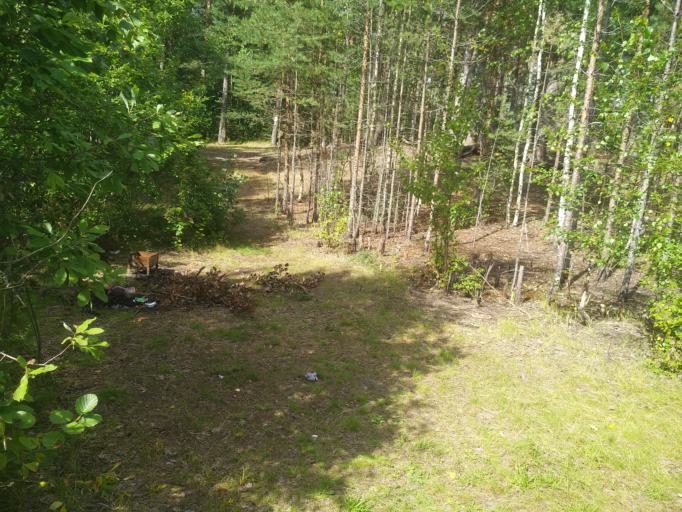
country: RU
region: Leningrad
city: Sapernoye
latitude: 60.6717
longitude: 29.9277
